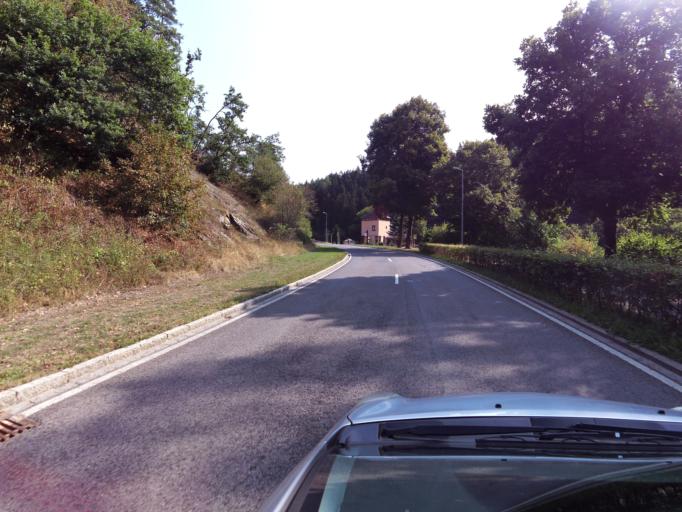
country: LU
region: Diekirch
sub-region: Canton de Wiltz
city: Esch-sur-Sure
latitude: 49.9067
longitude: 5.9413
